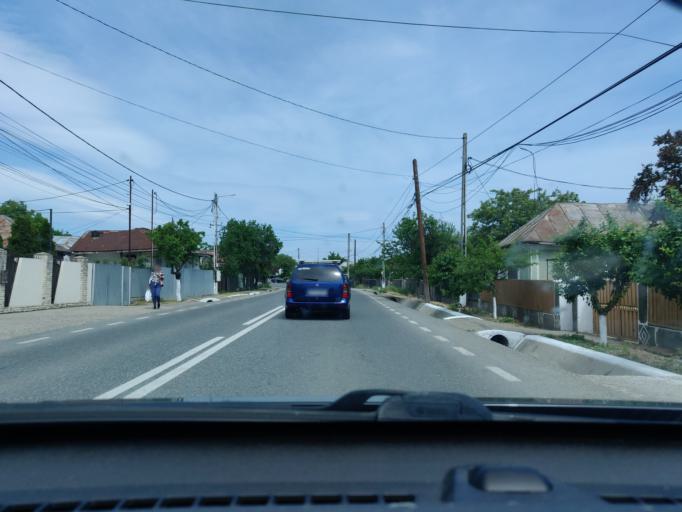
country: RO
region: Vrancea
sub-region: Comuna Bolotesti
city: Gagesti
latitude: 45.8591
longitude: 27.0503
